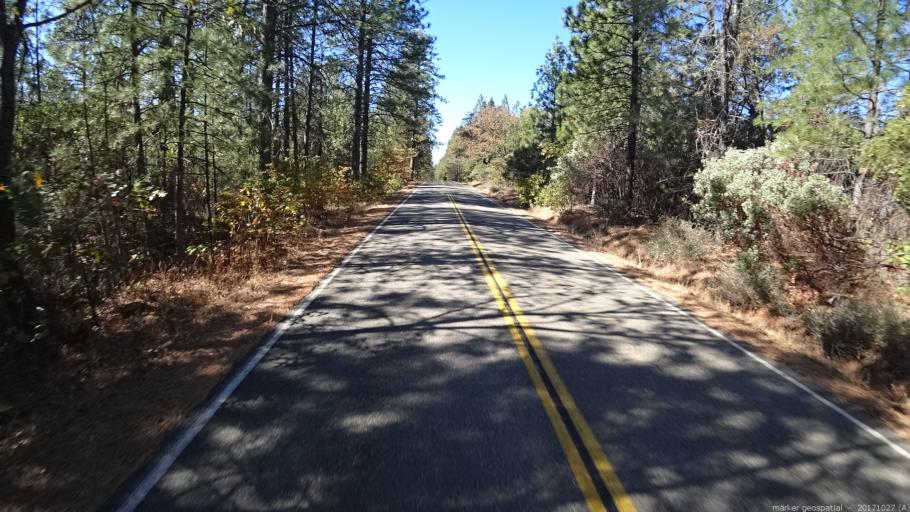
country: US
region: California
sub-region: Shasta County
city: Shingletown
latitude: 40.7005
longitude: -121.9896
